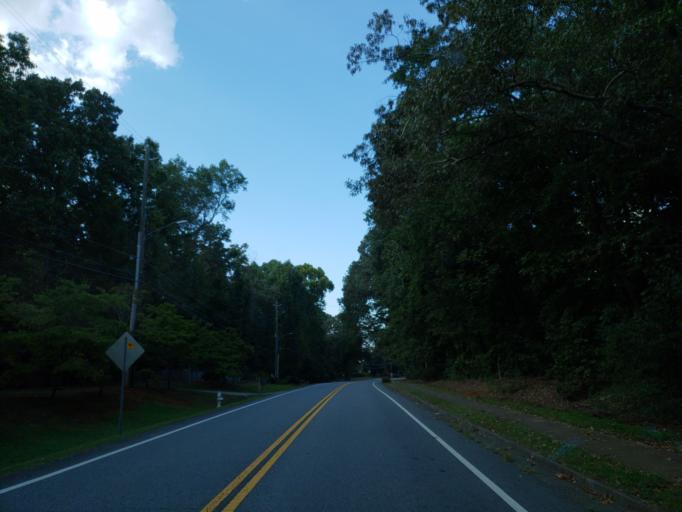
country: US
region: Georgia
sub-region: Fulton County
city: Roswell
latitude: 34.0618
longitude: -84.3419
